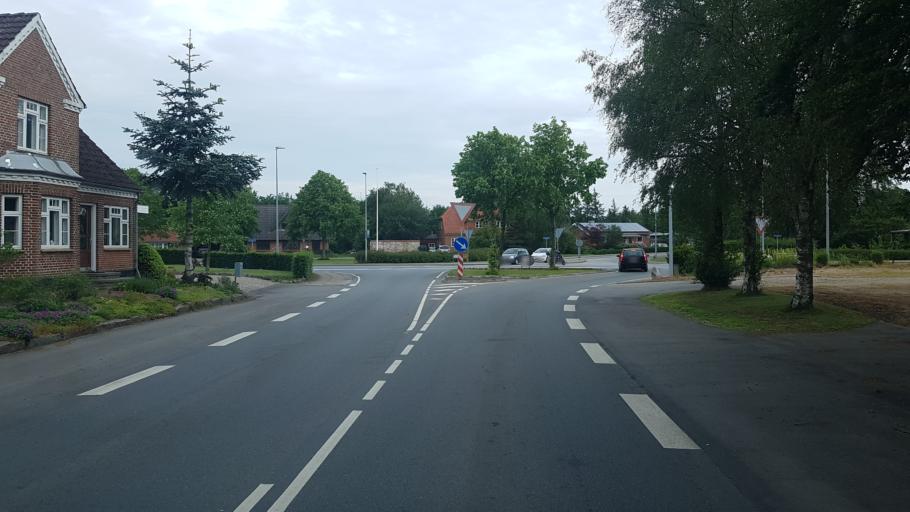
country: DK
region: South Denmark
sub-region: Vejen Kommune
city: Brorup
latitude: 55.4414
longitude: 9.0029
